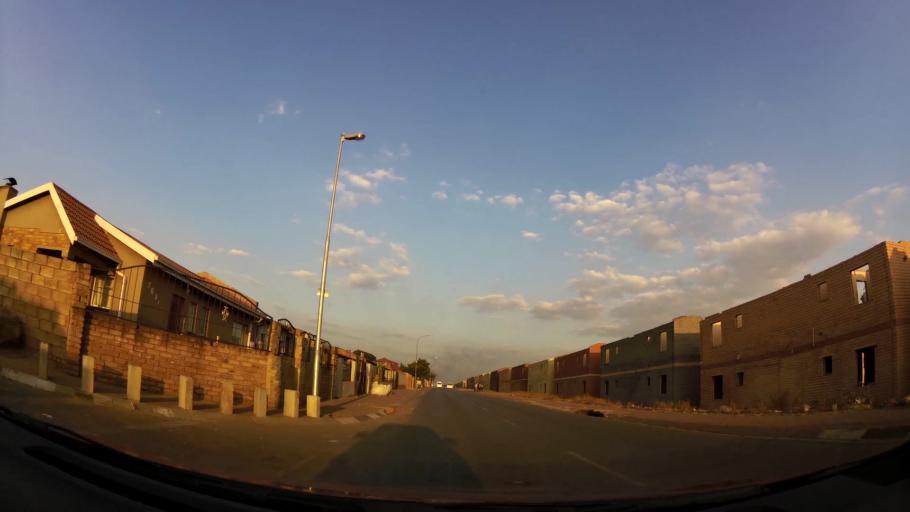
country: ZA
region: Gauteng
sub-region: City of Johannesburg Metropolitan Municipality
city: Soweto
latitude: -26.2326
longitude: 27.8970
